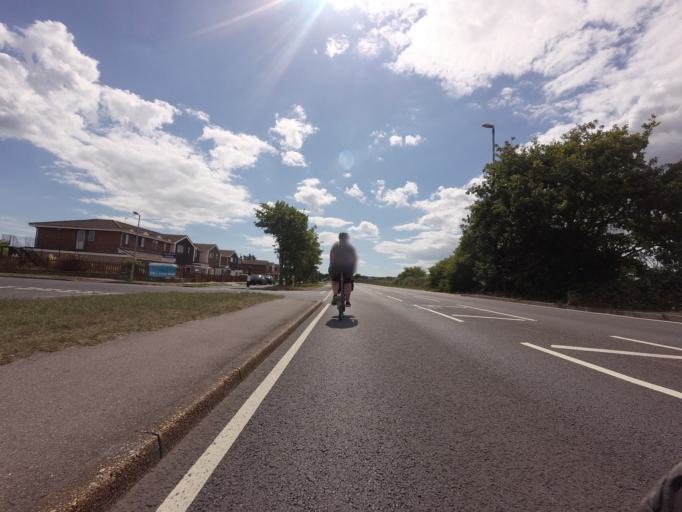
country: GB
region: England
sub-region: East Sussex
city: Pevensey
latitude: 50.8090
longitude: 0.3426
